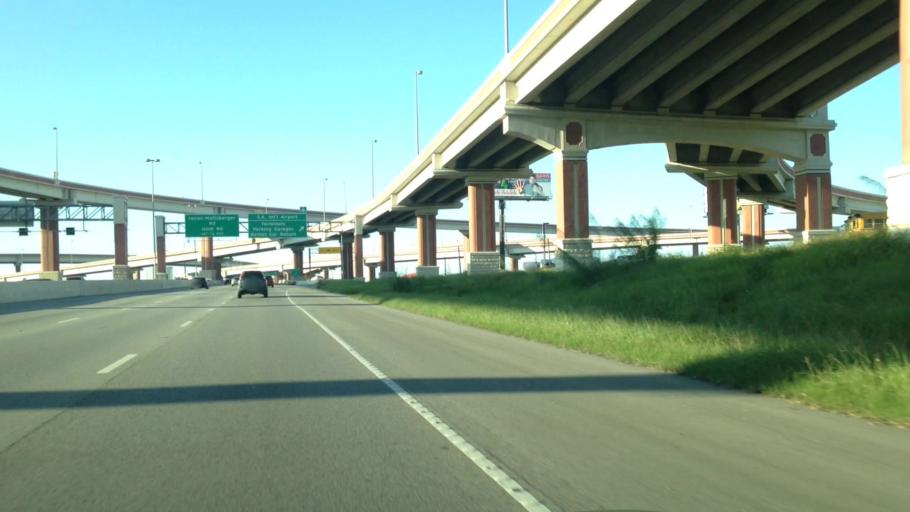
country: US
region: Texas
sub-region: Bexar County
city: Alamo Heights
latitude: 29.5173
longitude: -98.4782
